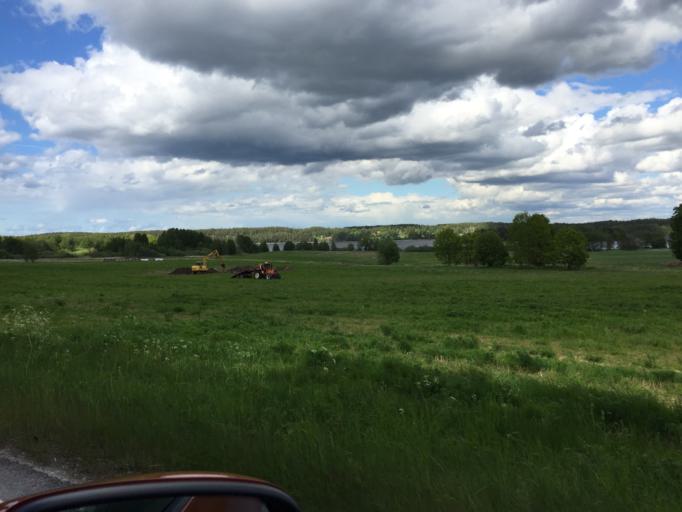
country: SE
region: OEstergoetland
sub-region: Finspangs Kommun
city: Finspang
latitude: 58.6537
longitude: 15.8114
